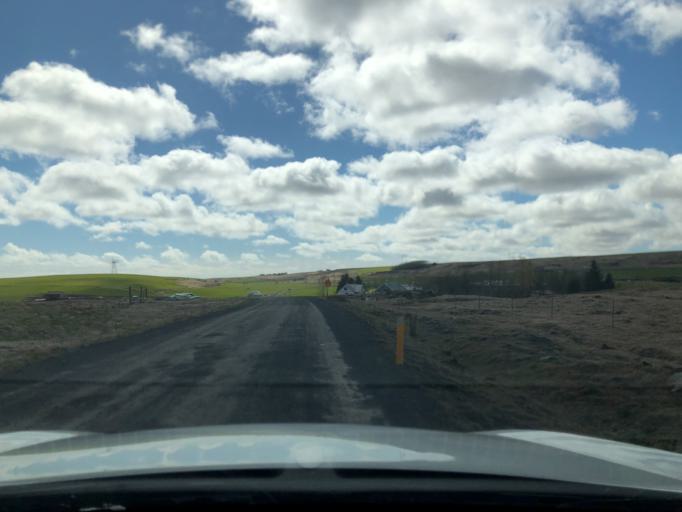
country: IS
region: South
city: Selfoss
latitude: 63.9272
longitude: -20.6740
